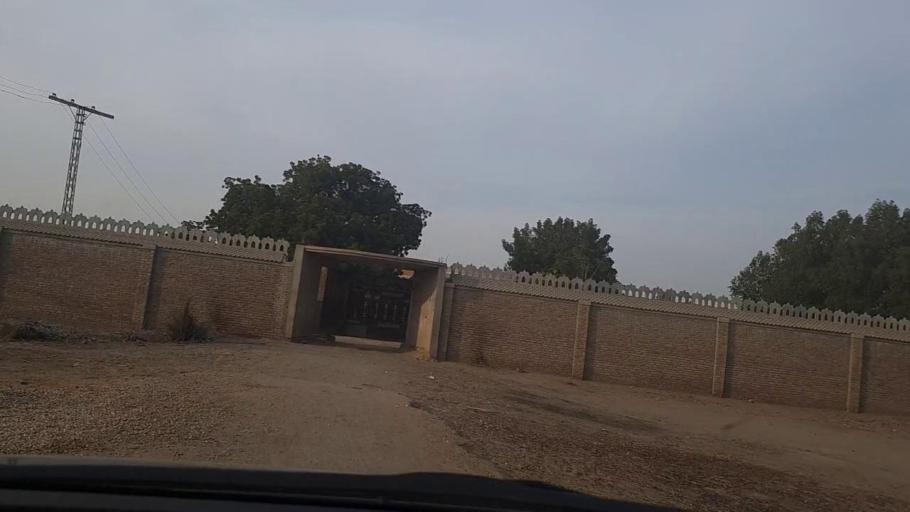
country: PK
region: Sindh
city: Daulatpur
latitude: 26.3377
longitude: 68.0197
